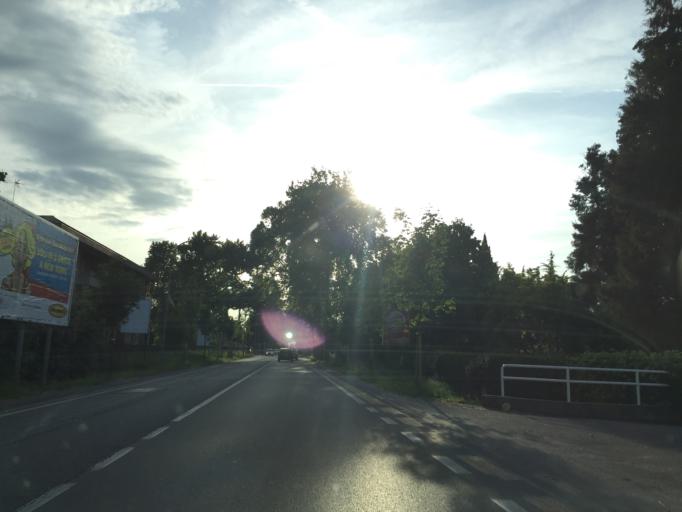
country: IT
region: Friuli Venezia Giulia
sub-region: Provincia di Pordenone
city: Porcia
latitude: 45.9672
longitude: 12.6340
